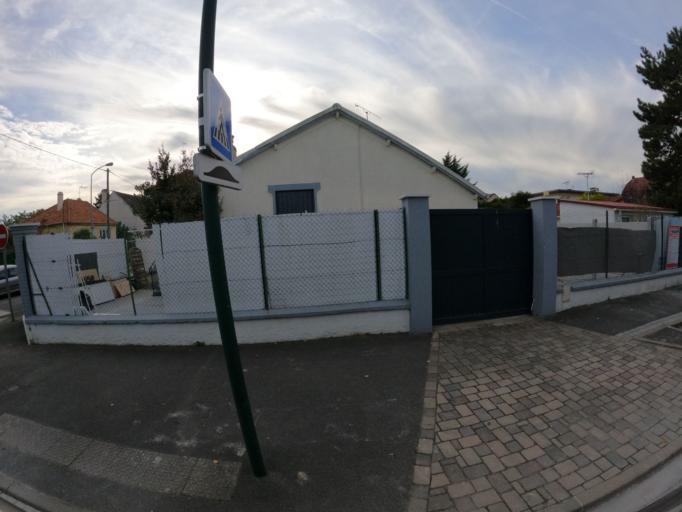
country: FR
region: Ile-de-France
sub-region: Departement de Seine-et-Marne
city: Pontault-Combault
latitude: 48.7982
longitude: 2.6076
